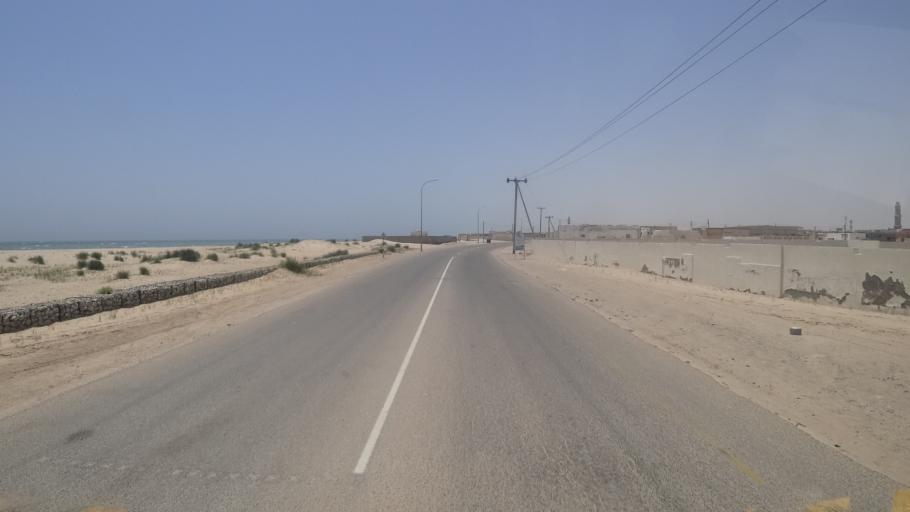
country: OM
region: Ash Sharqiyah
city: Sur
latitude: 22.0888
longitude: 59.6895
